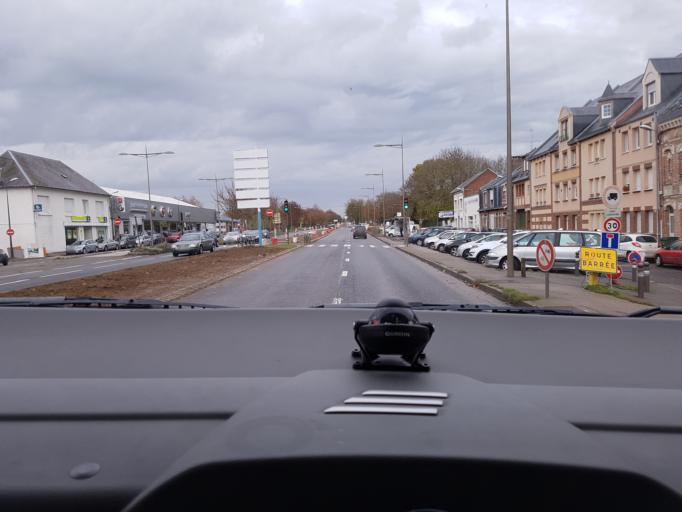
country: FR
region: Picardie
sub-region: Departement de la Somme
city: Amiens
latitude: 49.8953
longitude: 2.3100
